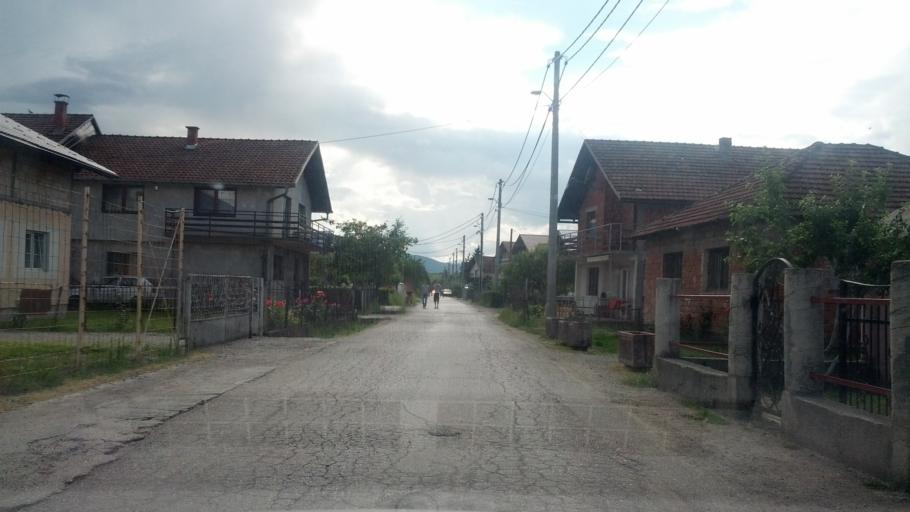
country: BA
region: Federation of Bosnia and Herzegovina
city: Bihac
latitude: 44.8407
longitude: 15.8818
